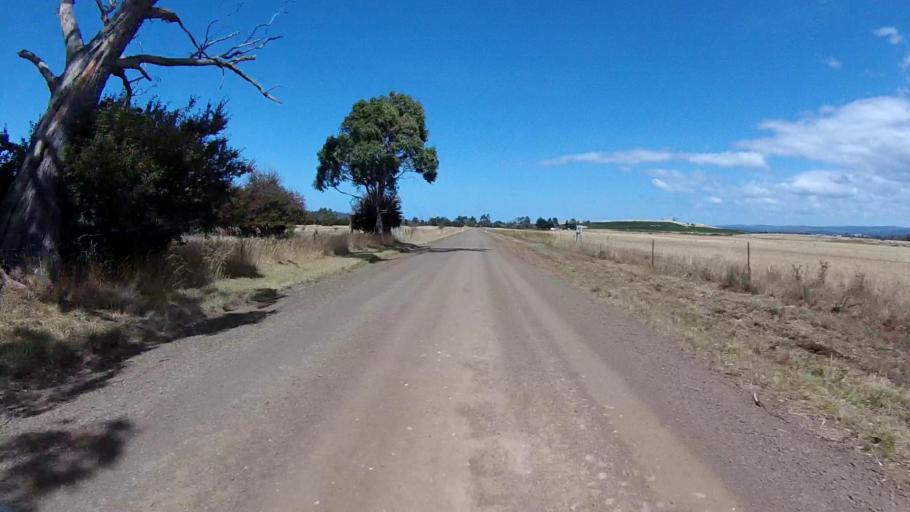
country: AU
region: Tasmania
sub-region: Break O'Day
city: St Helens
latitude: -41.9969
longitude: 148.0672
